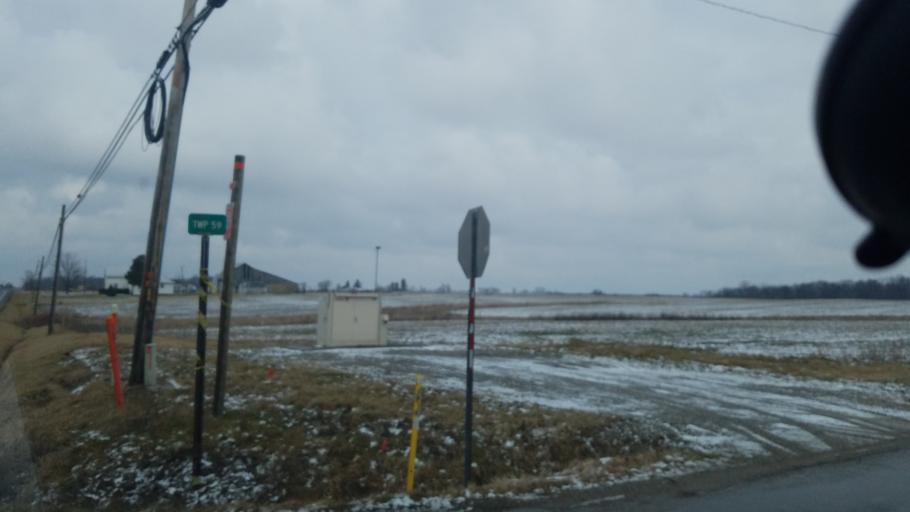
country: US
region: Ohio
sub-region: Morrow County
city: Mount Gilead
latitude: 40.6251
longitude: -82.8228
